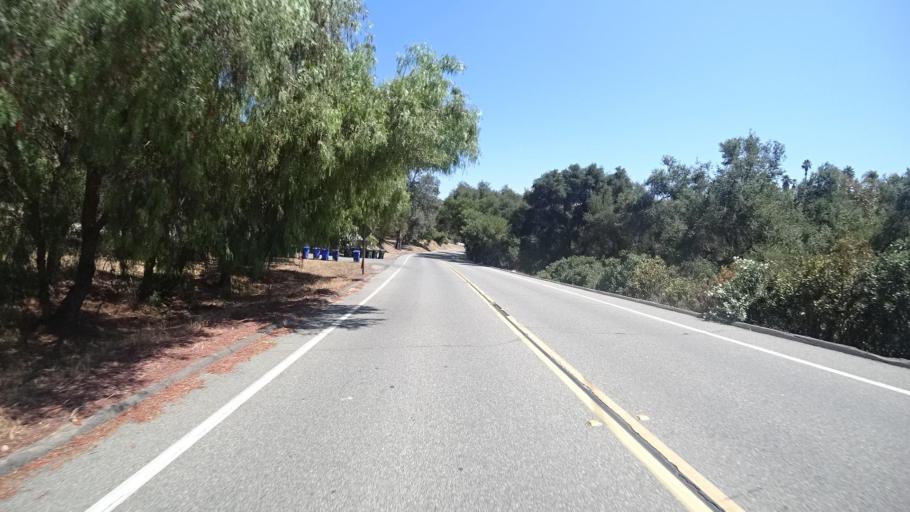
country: US
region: California
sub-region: San Diego County
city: Fallbrook
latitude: 33.3559
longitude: -117.2005
